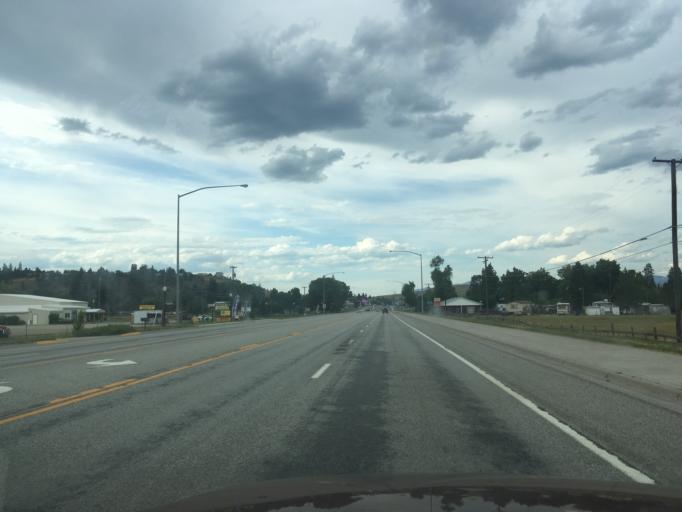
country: US
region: Montana
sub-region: Missoula County
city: Lolo
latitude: 46.7512
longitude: -114.0828
